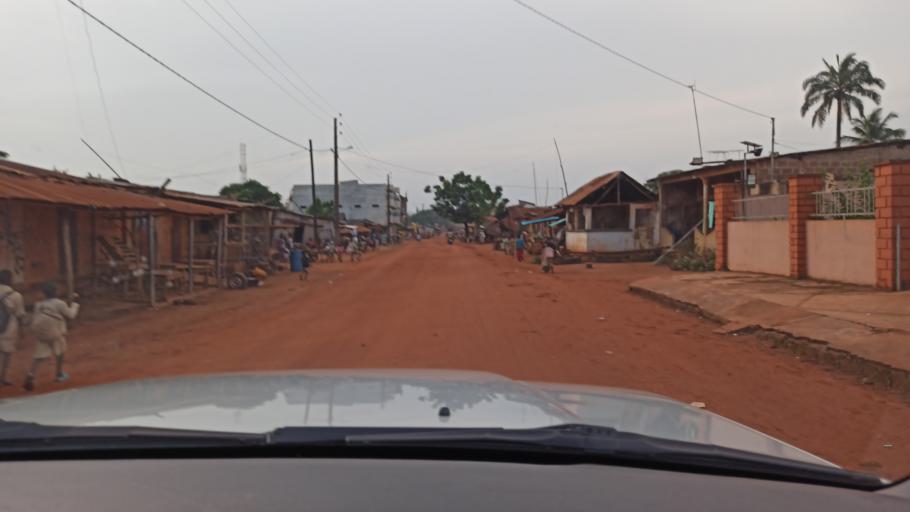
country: BJ
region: Queme
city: Porto-Novo
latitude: 6.5280
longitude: 2.6676
